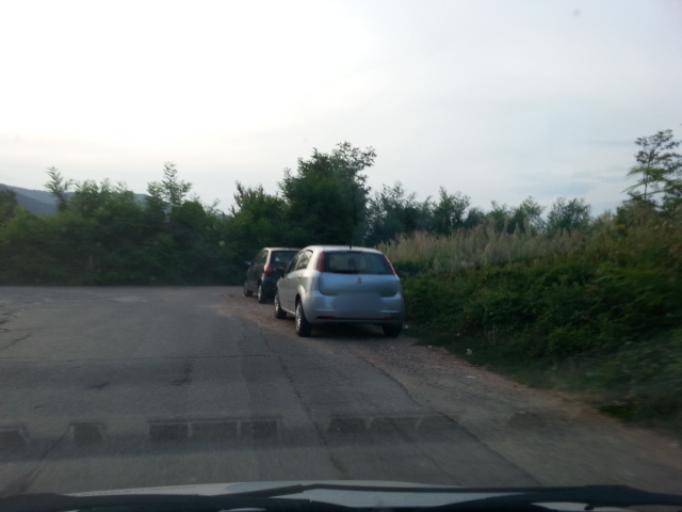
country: IT
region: Piedmont
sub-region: Provincia di Torino
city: Piossasco
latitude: 44.9925
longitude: 7.4766
